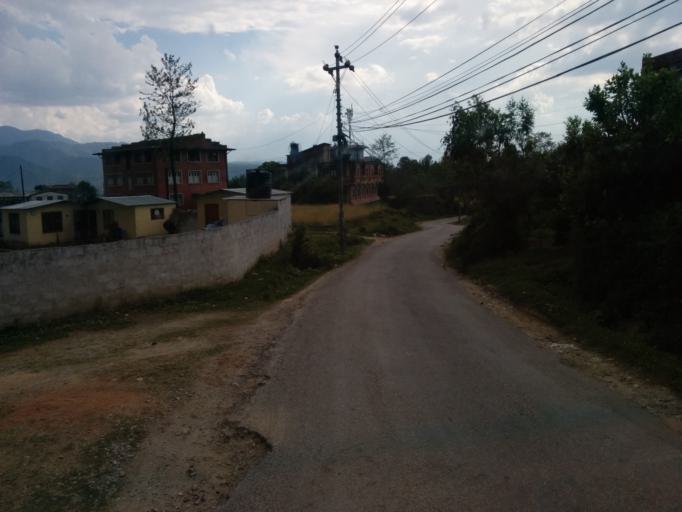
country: NP
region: Central Region
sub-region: Bagmati Zone
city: Bhaktapur
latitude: 27.6961
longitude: 85.4645
